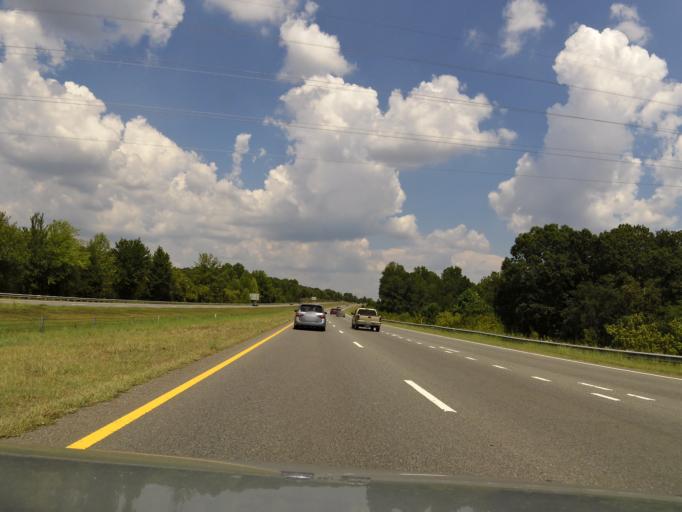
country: US
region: North Carolina
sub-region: Cleveland County
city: White Plains
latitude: 35.2501
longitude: -81.4022
